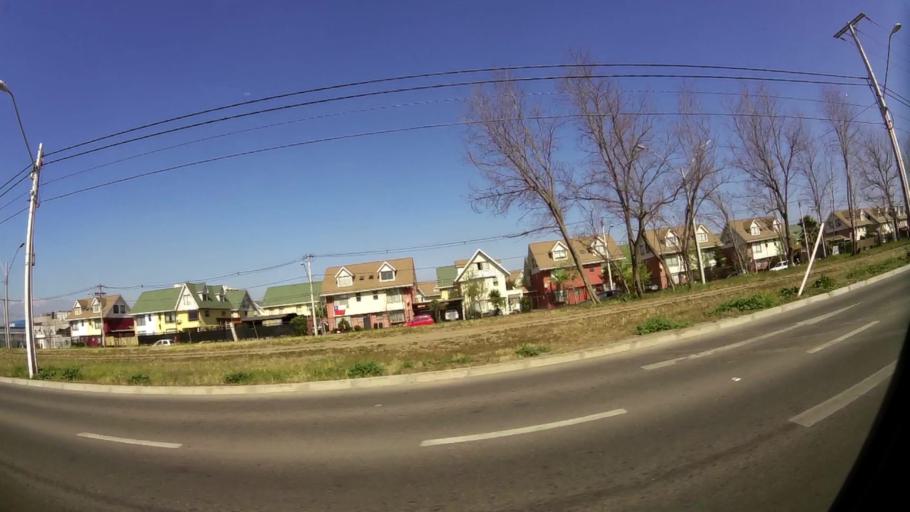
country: CL
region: Santiago Metropolitan
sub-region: Provincia de Santiago
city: Lo Prado
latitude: -33.4799
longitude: -70.7593
